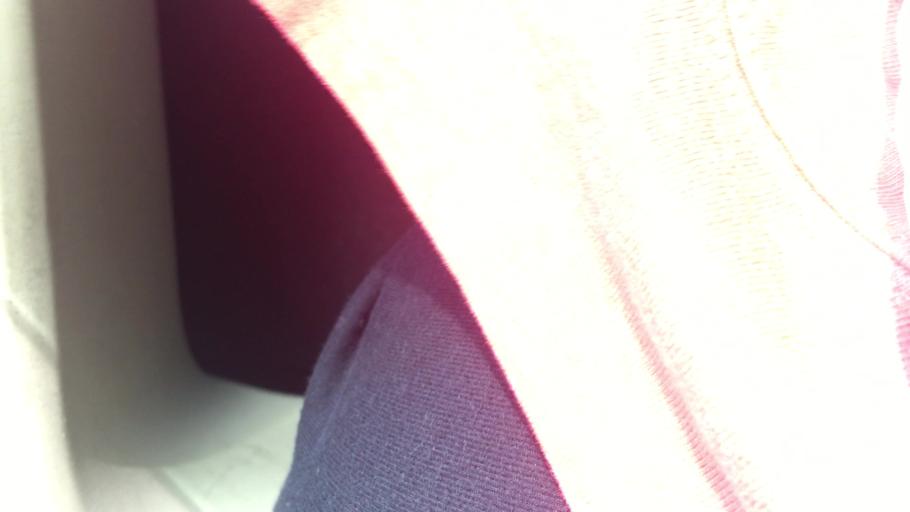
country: IT
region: Molise
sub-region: Provincia di Isernia
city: Carovilli
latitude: 41.7342
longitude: 14.2639
